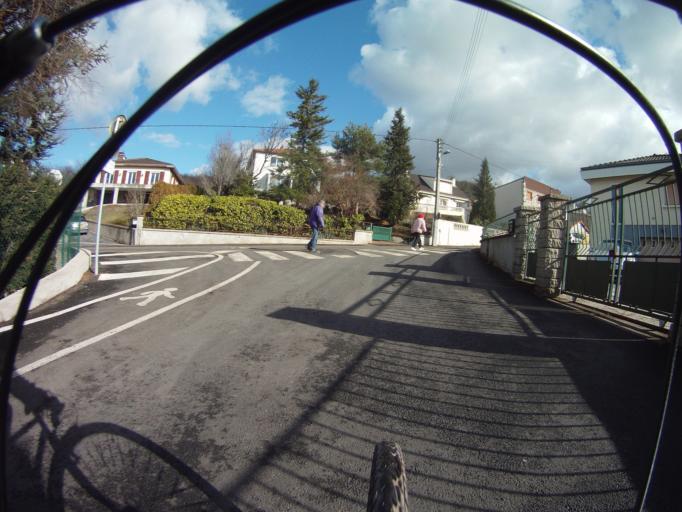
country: FR
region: Auvergne
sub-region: Departement du Puy-de-Dome
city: Aubiere
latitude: 45.7432
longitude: 3.1101
